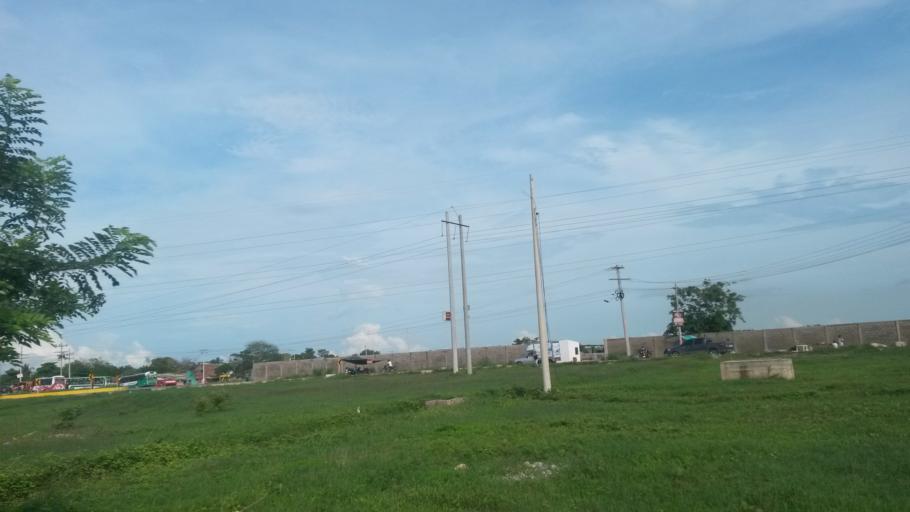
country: CO
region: Bolivar
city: Cartagena
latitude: 10.4070
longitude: -75.4490
